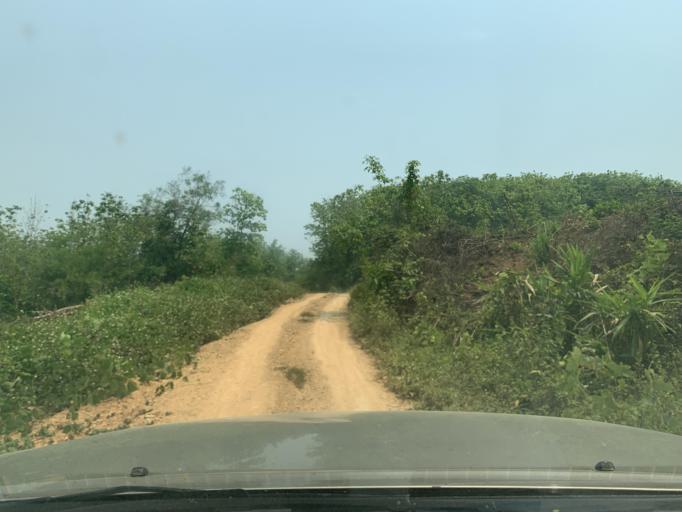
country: LA
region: Louangphabang
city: Xiang Ngeun
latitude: 19.8259
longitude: 102.2151
